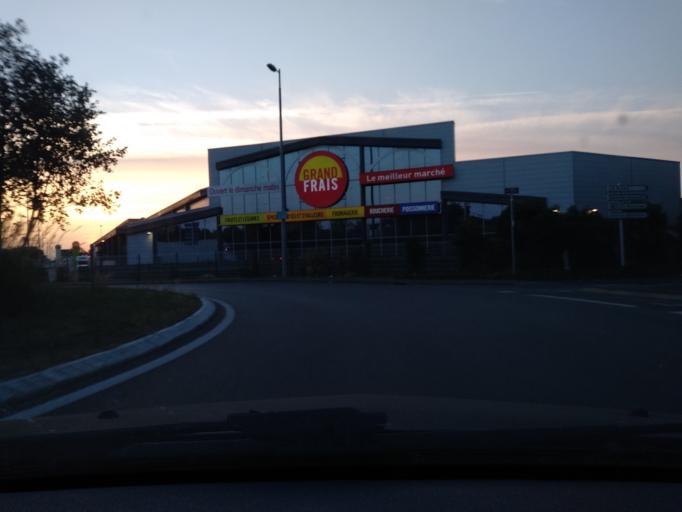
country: FR
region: Centre
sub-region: Departement d'Indre-et-Loire
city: Tours
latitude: 47.3748
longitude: 0.6714
